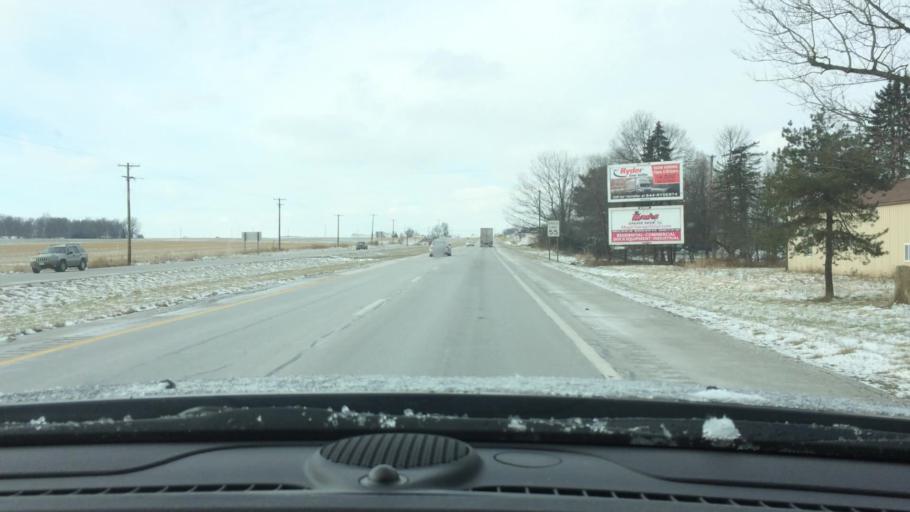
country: US
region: Ohio
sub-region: Wayne County
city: Dalton
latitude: 40.7980
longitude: -81.6593
